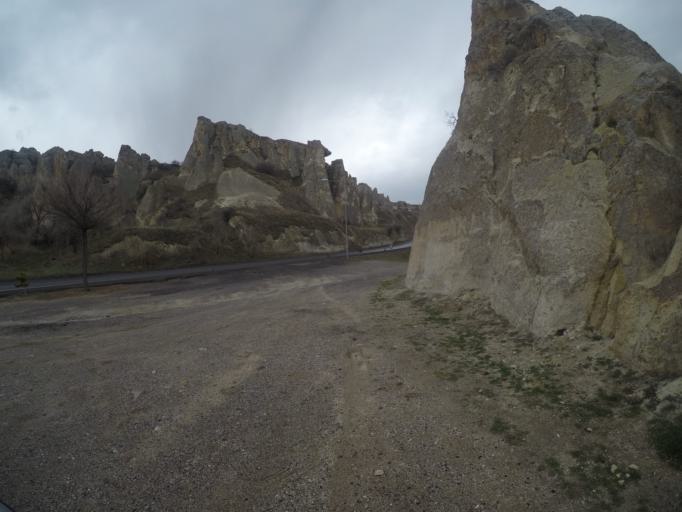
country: TR
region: Nevsehir
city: Urgub
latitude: 38.6340
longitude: 34.8939
